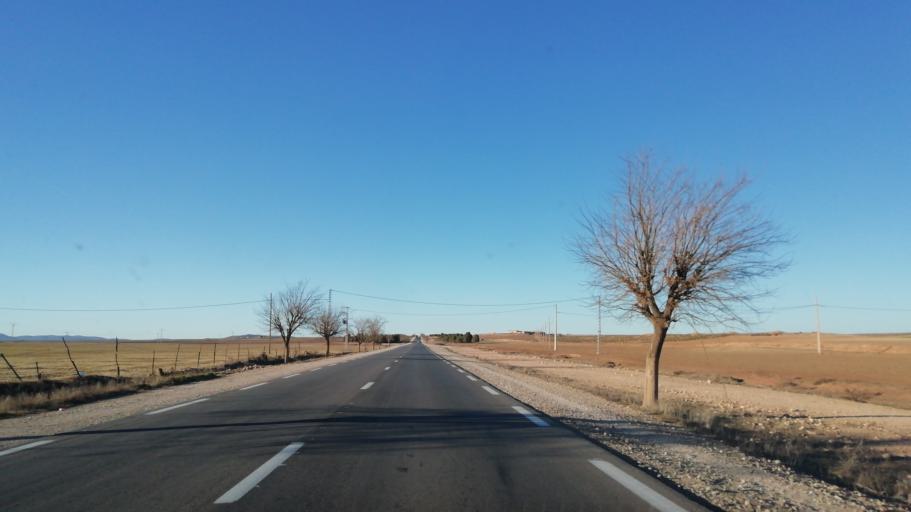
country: DZ
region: Tlemcen
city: Sebdou
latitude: 34.5206
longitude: -1.2890
